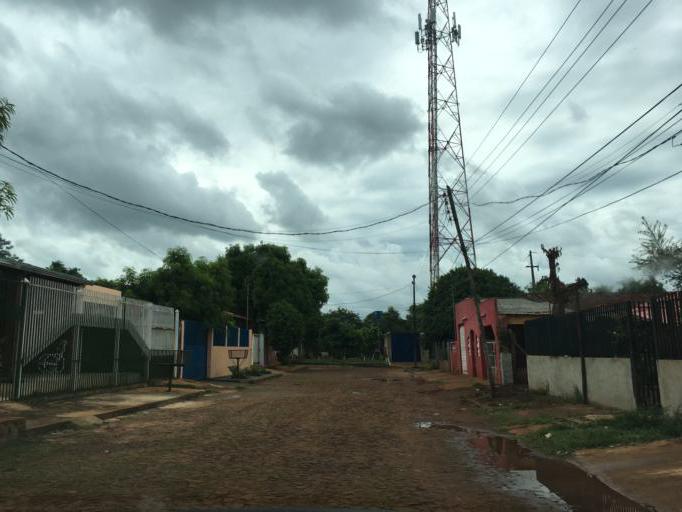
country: PY
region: Alto Parana
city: Ciudad del Este
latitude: -25.4186
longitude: -54.6404
